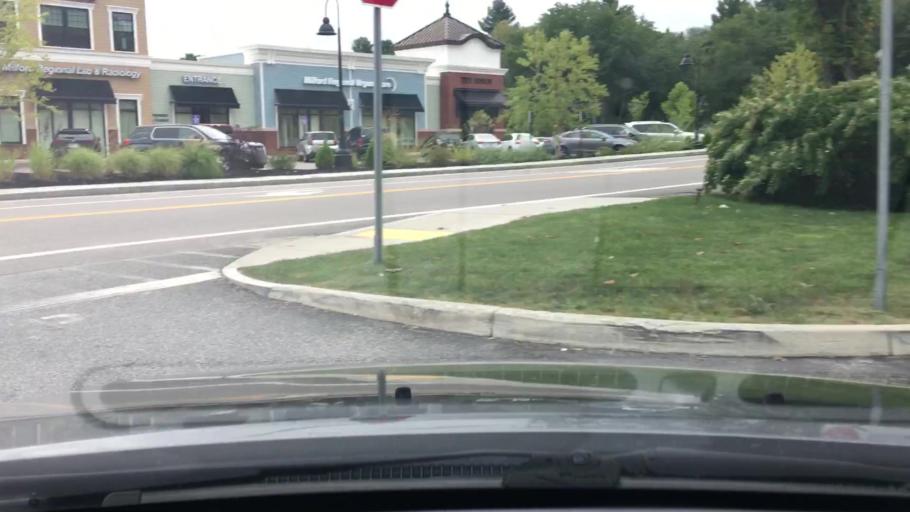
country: US
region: Massachusetts
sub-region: Middlesex County
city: Hopkinton
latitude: 42.2168
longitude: -71.5412
